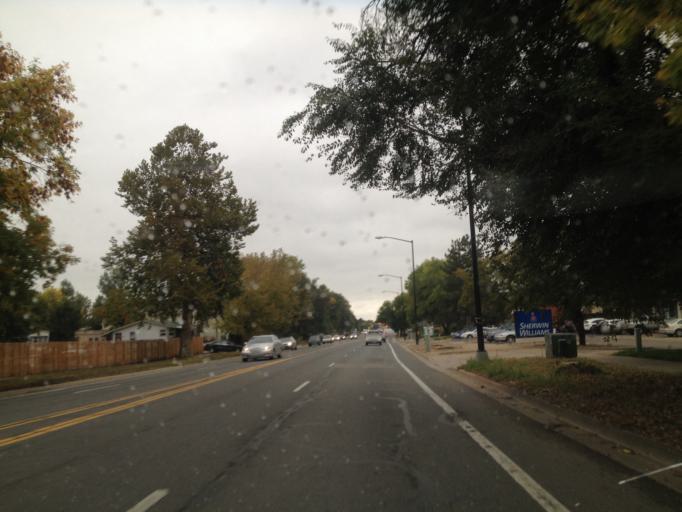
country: US
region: Colorado
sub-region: Boulder County
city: Boulder
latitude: 40.0292
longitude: -105.2526
